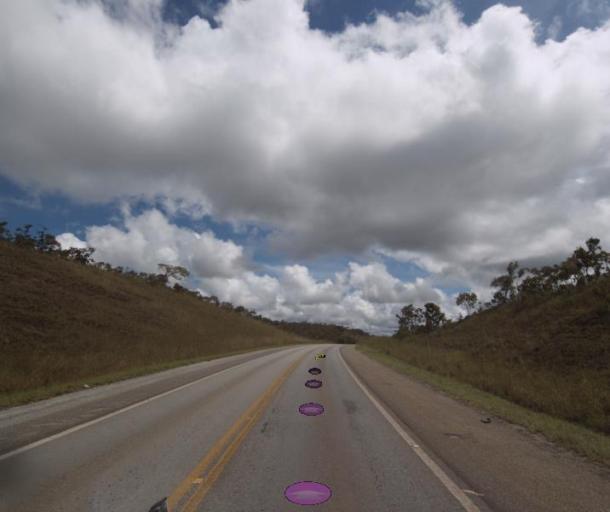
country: BR
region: Goias
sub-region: Pirenopolis
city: Pirenopolis
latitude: -15.7730
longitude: -48.5551
